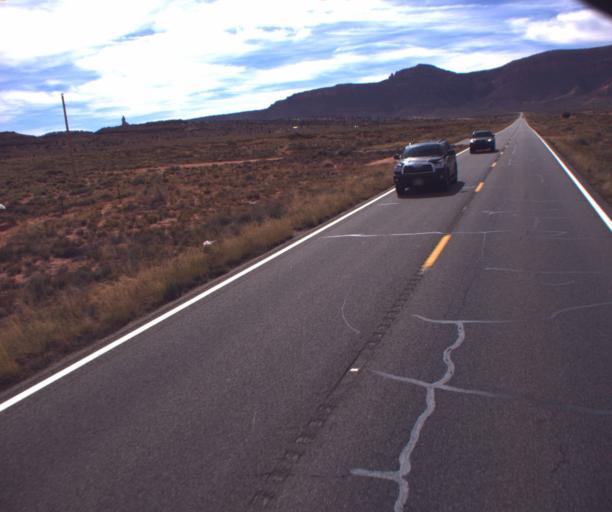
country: US
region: Arizona
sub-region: Navajo County
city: Kayenta
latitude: 36.8729
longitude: -110.2585
